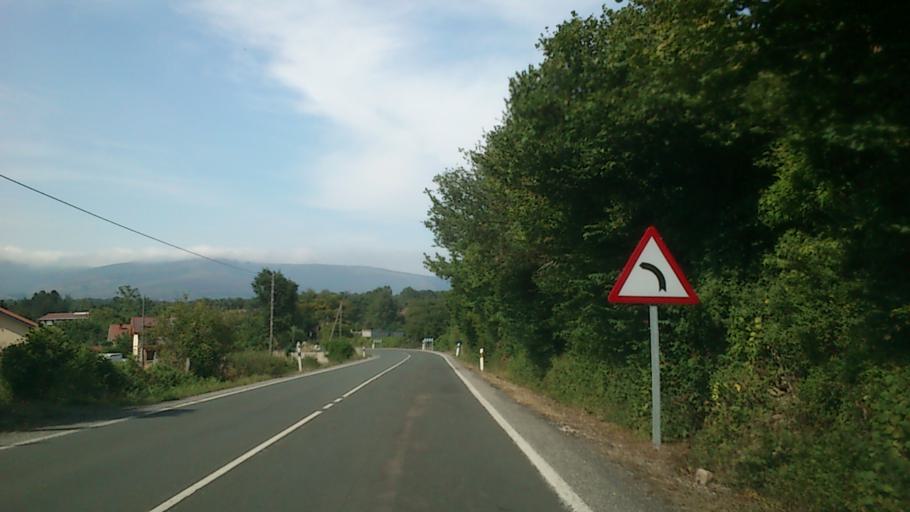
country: ES
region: Castille and Leon
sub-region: Provincia de Burgos
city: Espinosa de los Monteros
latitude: 43.0571
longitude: -3.4921
